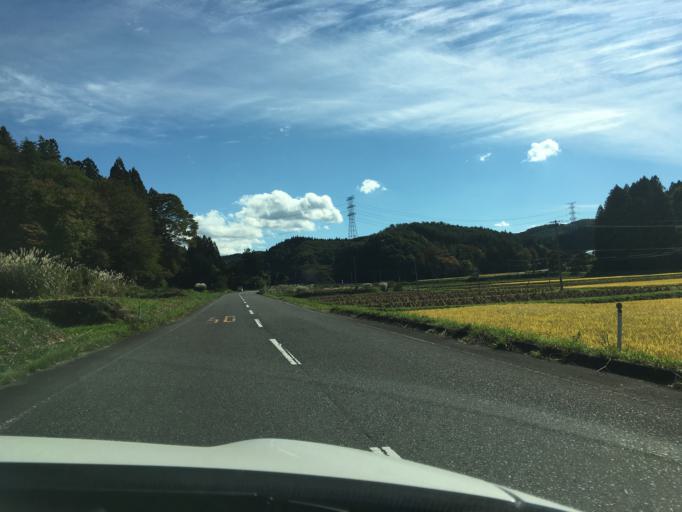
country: JP
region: Fukushima
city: Ishikawa
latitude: 37.1737
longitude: 140.5923
